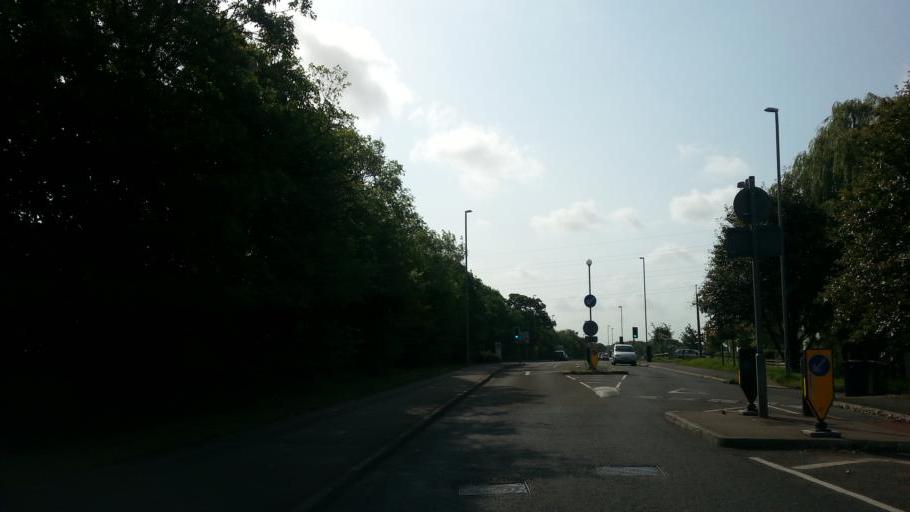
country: GB
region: England
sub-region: Cambridgeshire
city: Papworth Everard
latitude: 52.2434
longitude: -0.1136
